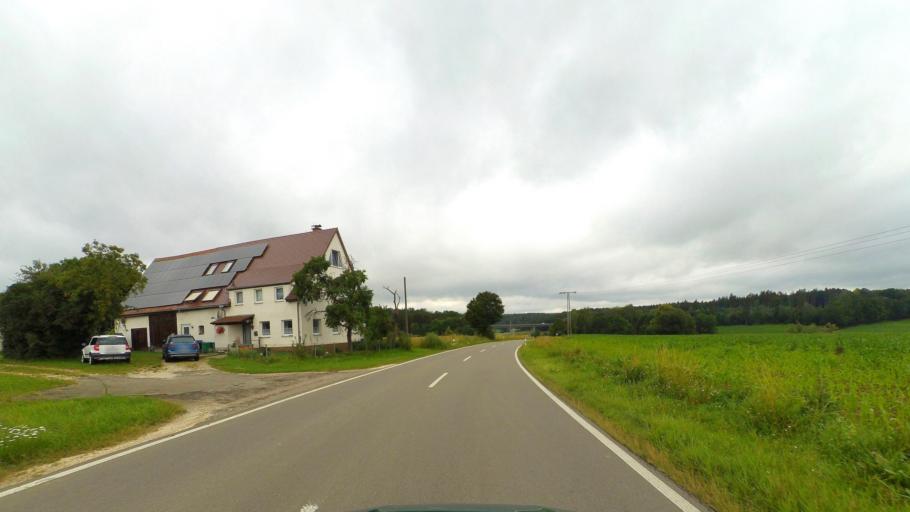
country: DE
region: Baden-Wuerttemberg
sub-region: Tuebingen Region
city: Nerenstetten
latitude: 48.5310
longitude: 10.0978
